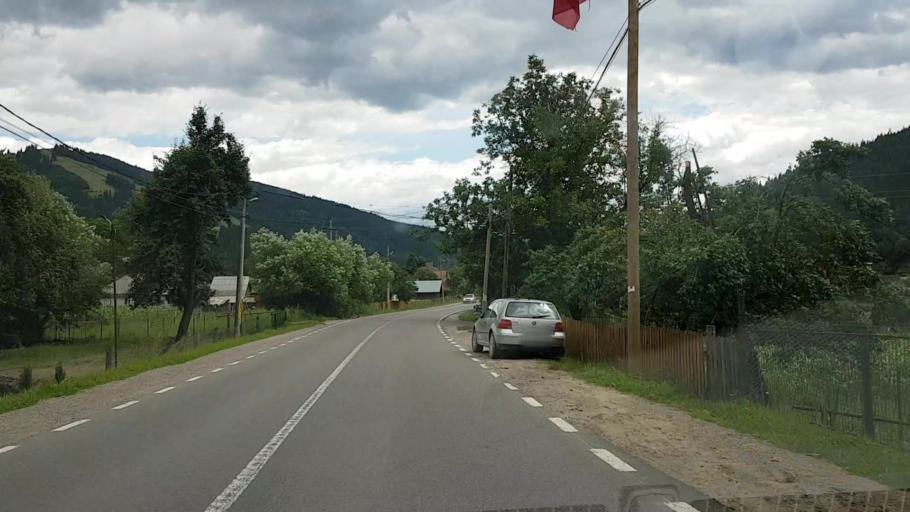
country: RO
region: Neamt
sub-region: Comuna Poiana Teiului
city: Poiana Teiului
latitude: 47.1171
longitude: 25.9194
